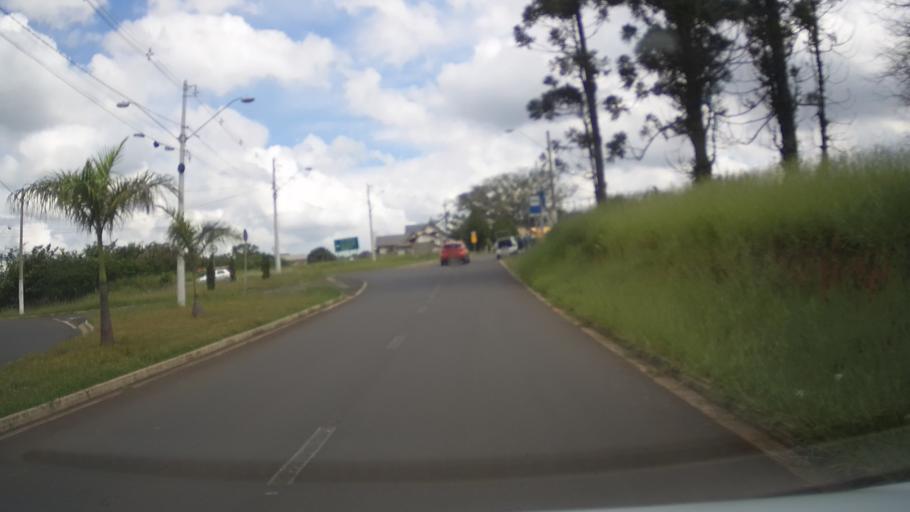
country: BR
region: Sao Paulo
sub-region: Valinhos
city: Valinhos
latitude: -22.9759
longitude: -46.9712
